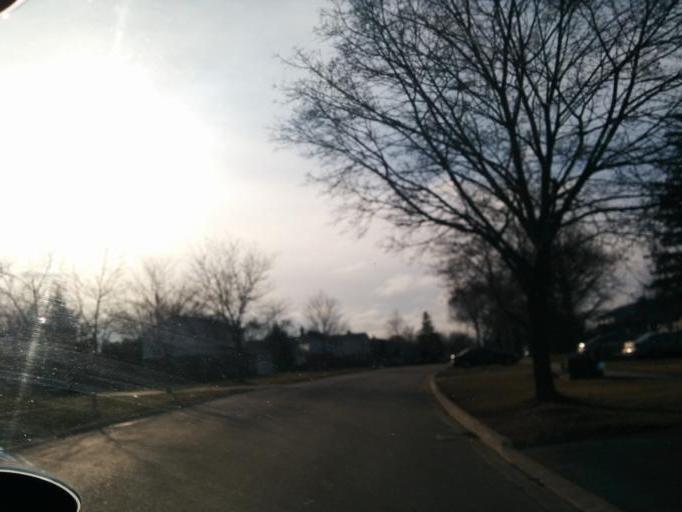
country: CA
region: Ontario
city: Mississauga
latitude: 43.5215
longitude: -79.6711
